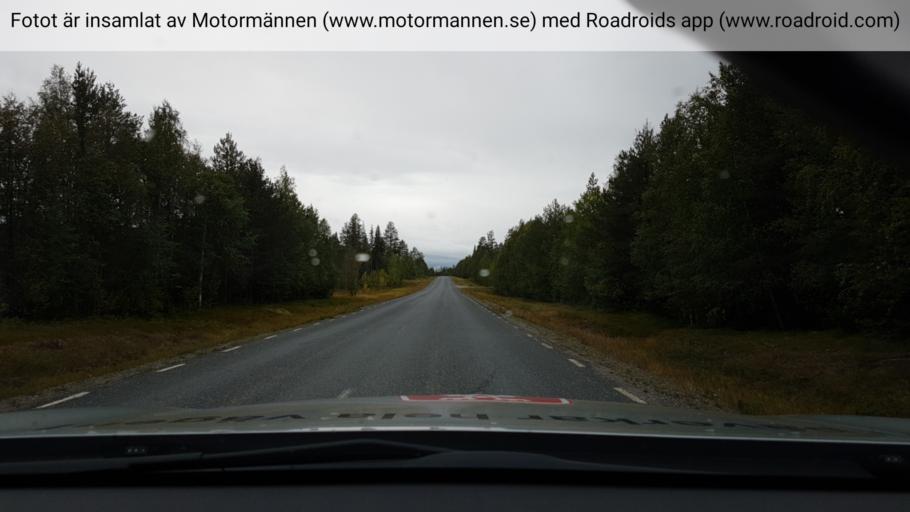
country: SE
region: Vaesterbotten
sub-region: Norsjo Kommun
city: Norsjoe
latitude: 65.3729
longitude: 19.6459
